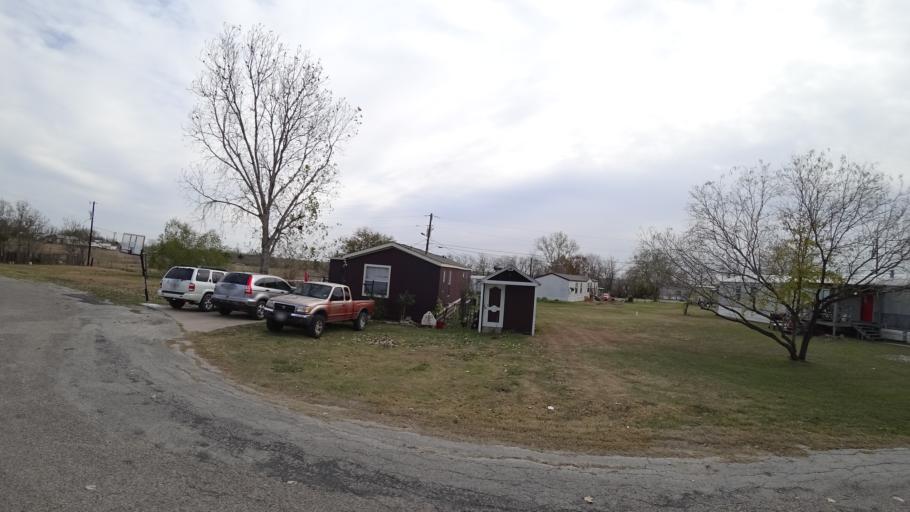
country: US
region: Texas
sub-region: Travis County
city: Garfield
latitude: 30.1491
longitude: -97.6669
